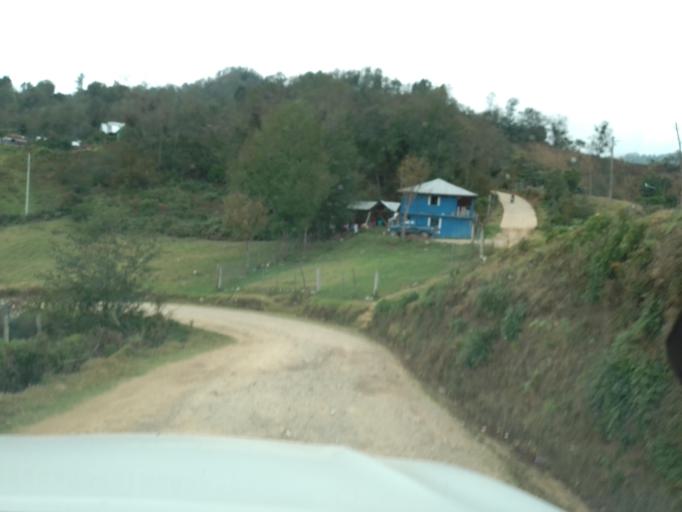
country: MX
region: Chiapas
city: Motozintla de Mendoza
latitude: 15.2194
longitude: -92.2312
